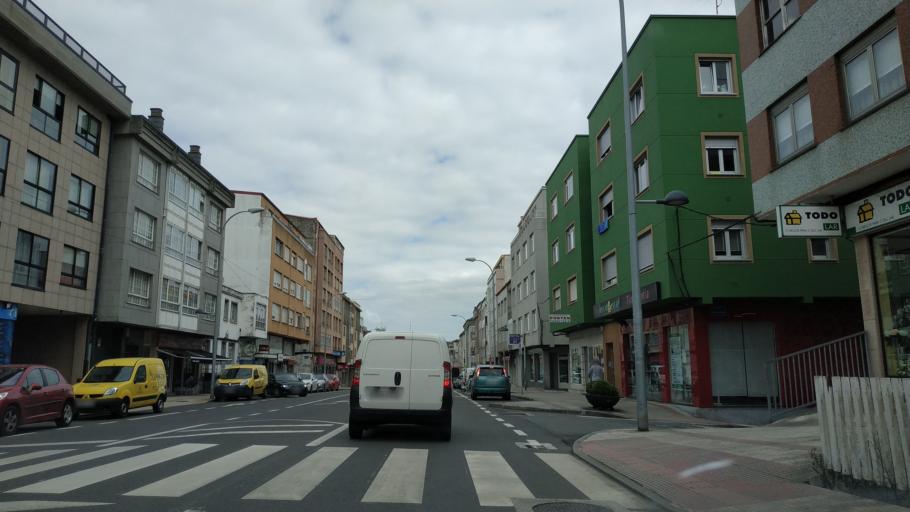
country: ES
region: Galicia
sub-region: Provincia da Coruna
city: Arteixo
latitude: 43.3042
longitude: -8.5119
